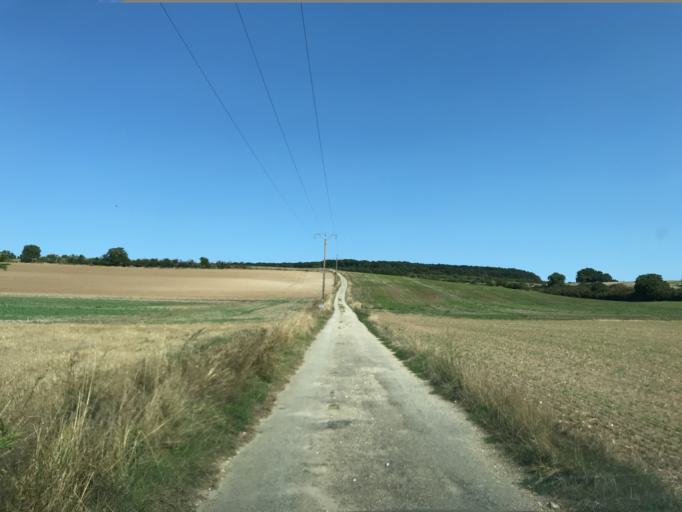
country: FR
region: Haute-Normandie
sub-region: Departement de l'Eure
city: Heudreville-sur-Eure
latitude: 49.1237
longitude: 1.2227
